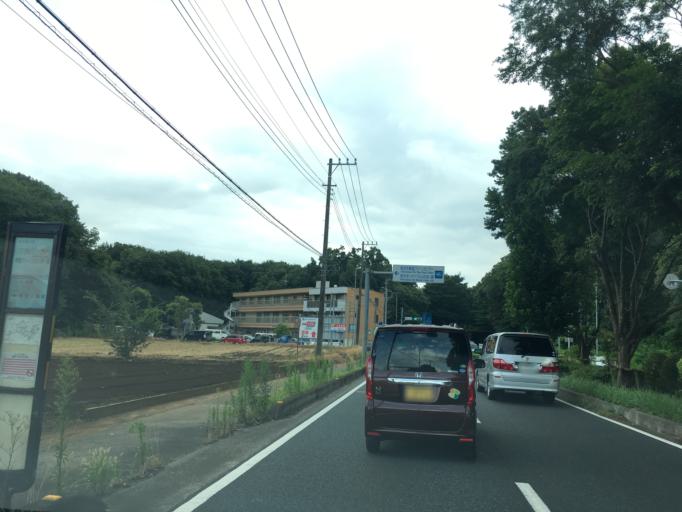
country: JP
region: Saitama
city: Tokorozawa
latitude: 35.8048
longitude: 139.4964
